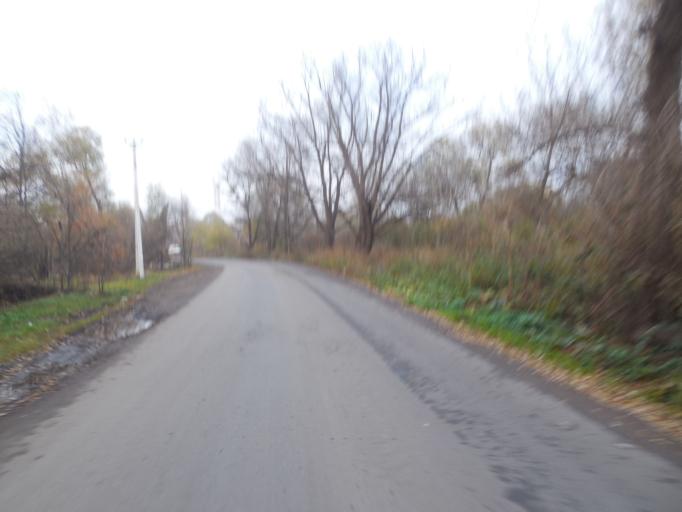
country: RU
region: Moskovskaya
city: Shcherbinka
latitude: 55.5113
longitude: 37.5818
